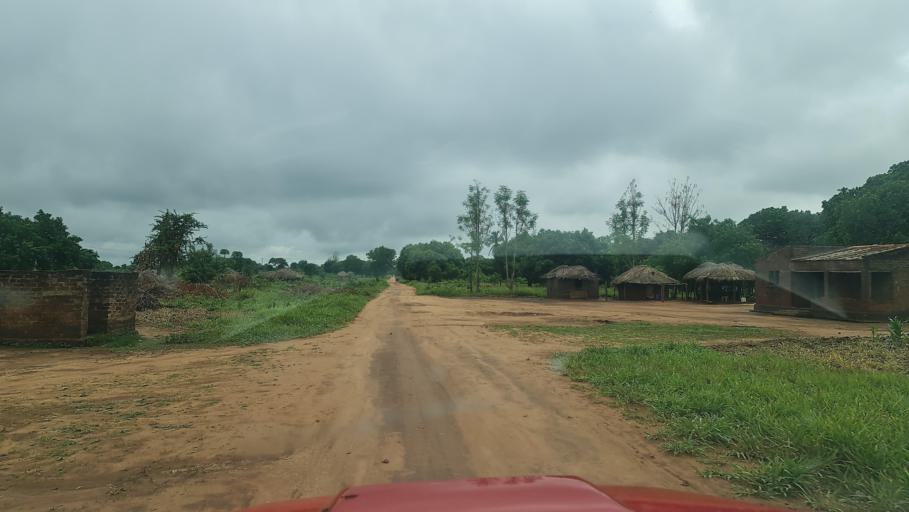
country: MW
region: Southern Region
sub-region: Nsanje District
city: Nsanje
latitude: -17.1798
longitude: 35.8939
